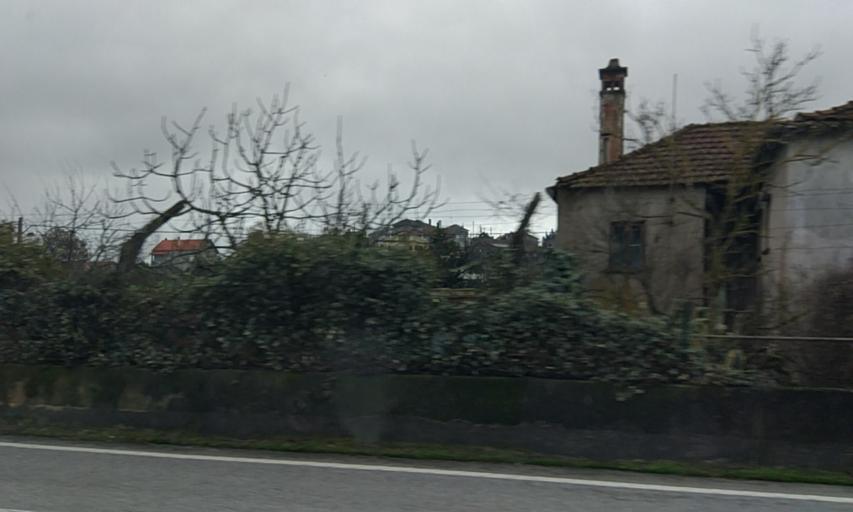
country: PT
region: Viseu
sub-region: Santa Comba Dao
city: Santa Comba Dao
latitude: 40.3578
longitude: -8.1425
